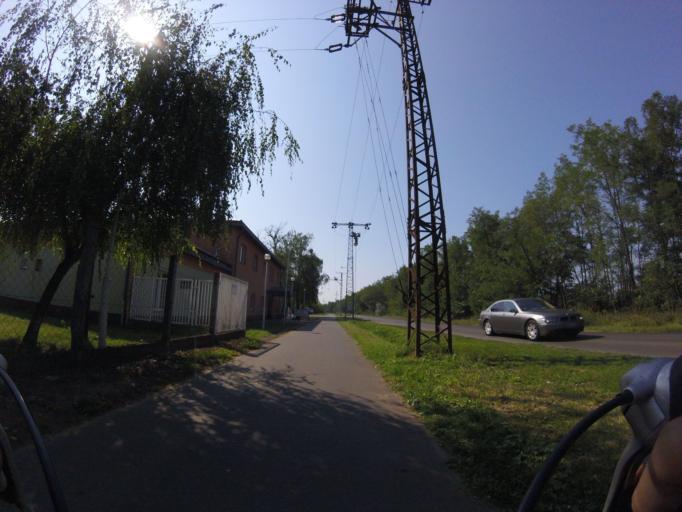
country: HU
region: Szabolcs-Szatmar-Bereg
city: Nyiregyhaza
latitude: 47.9801
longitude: 21.7050
